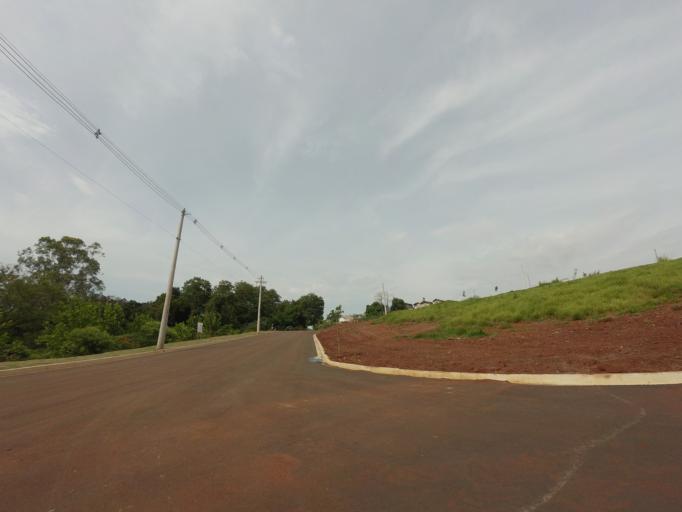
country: BR
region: Sao Paulo
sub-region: Piracicaba
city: Piracicaba
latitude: -22.7659
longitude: -47.5825
